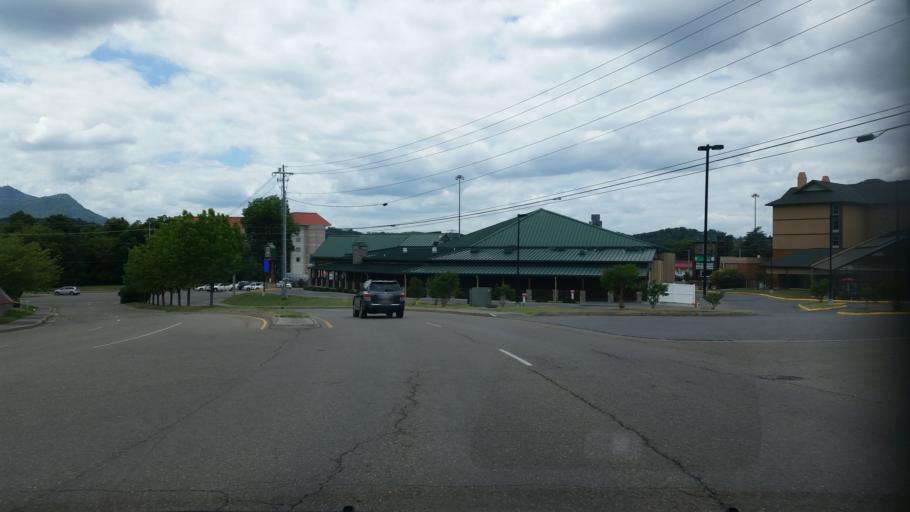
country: US
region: Tennessee
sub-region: Sevier County
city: Pigeon Forge
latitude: 35.8121
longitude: -83.5763
